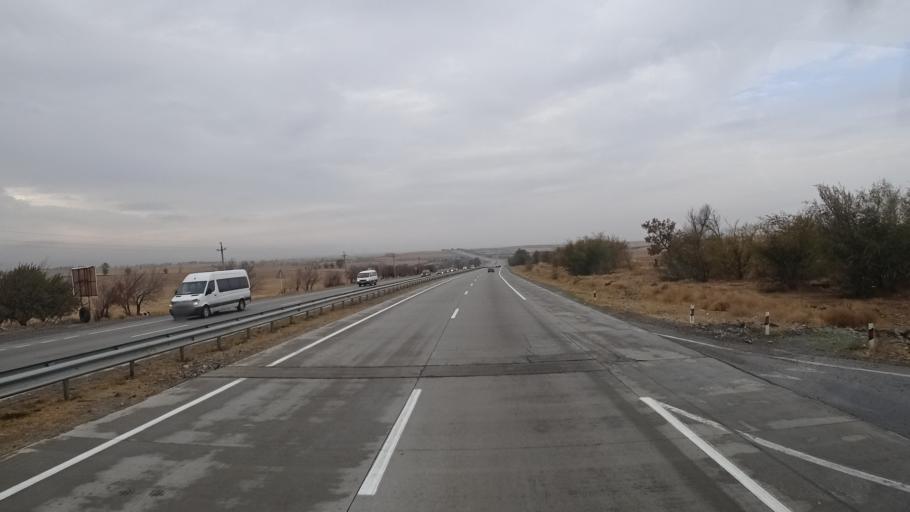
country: KZ
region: Ongtustik Qazaqstan
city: Sastobe
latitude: 42.4872
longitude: 69.9353
